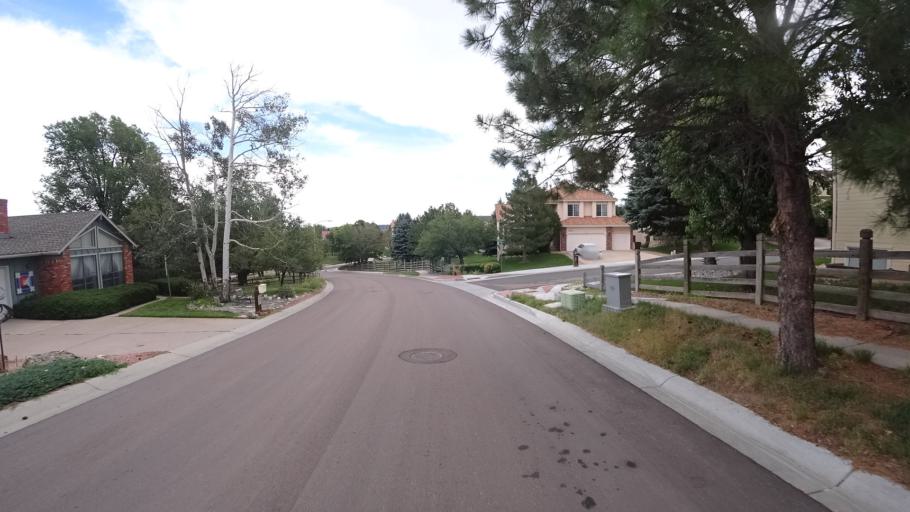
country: US
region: Colorado
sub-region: El Paso County
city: Colorado Springs
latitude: 38.9037
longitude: -104.8375
